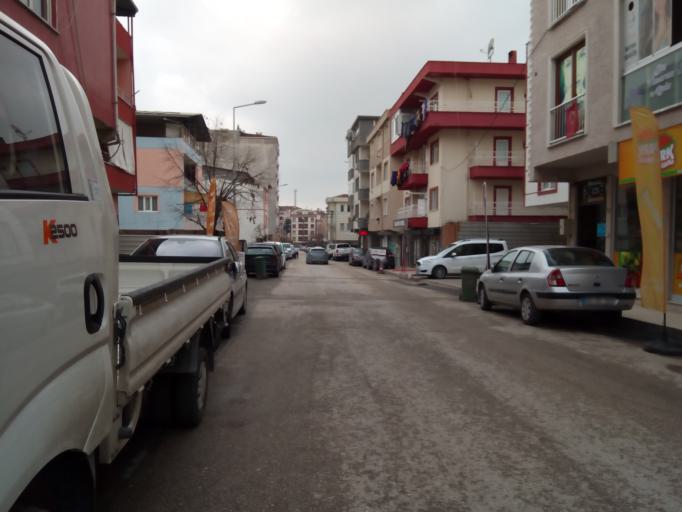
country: TR
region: Bursa
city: Niluefer
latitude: 40.2547
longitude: 28.9580
